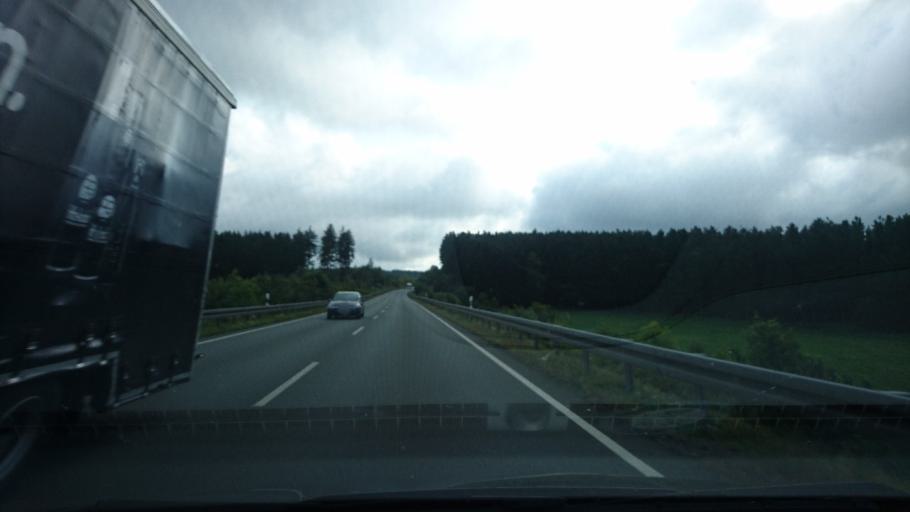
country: DE
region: Bavaria
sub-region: Upper Franconia
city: Selbitz
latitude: 50.3369
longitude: 11.7706
